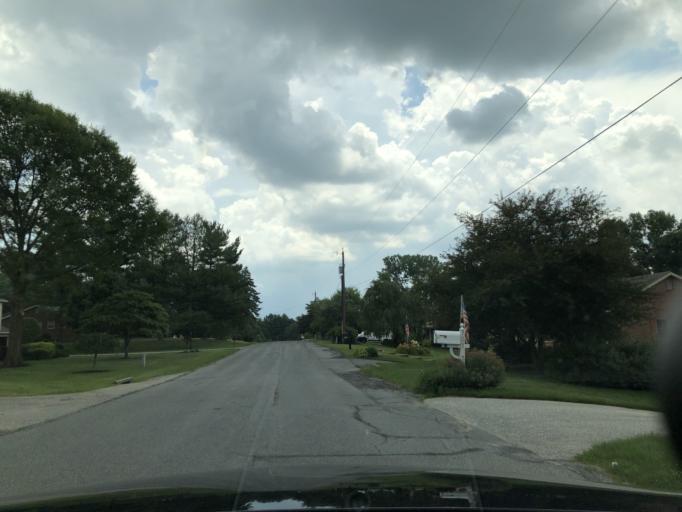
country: US
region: Maryland
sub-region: Carroll County
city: Westminster
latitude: 39.5556
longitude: -76.9870
